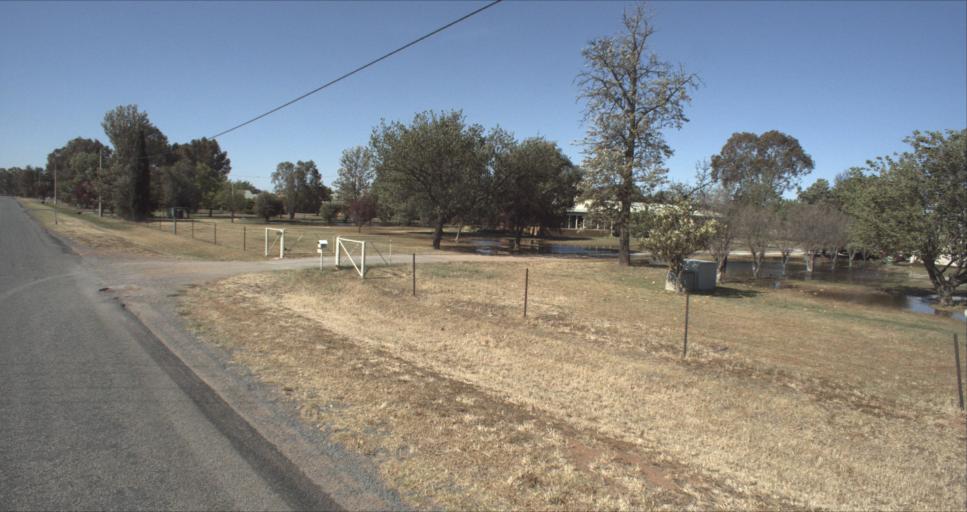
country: AU
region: New South Wales
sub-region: Leeton
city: Leeton
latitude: -34.5393
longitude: 146.4194
